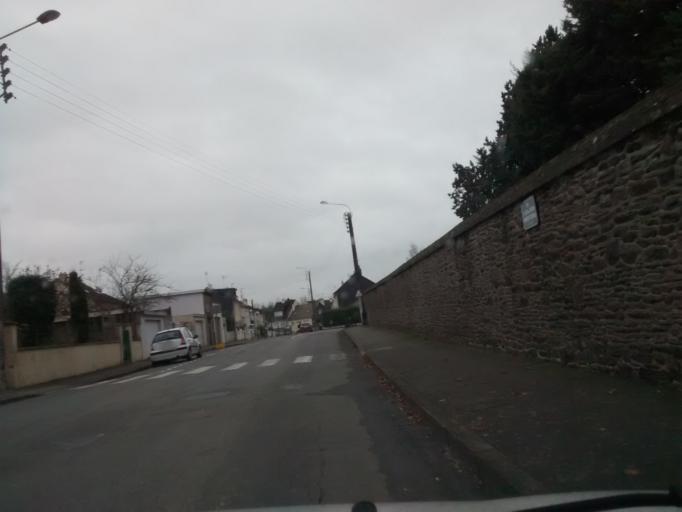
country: FR
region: Brittany
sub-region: Departement d'Ille-et-Vilaine
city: Chantepie
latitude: 48.1015
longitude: -1.6436
